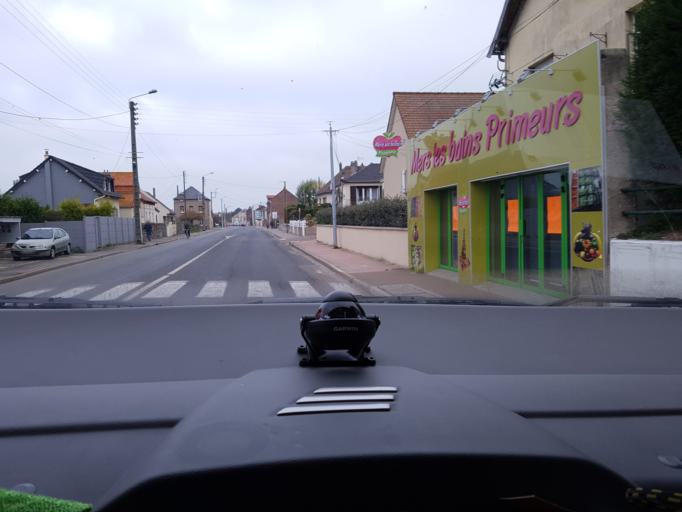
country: FR
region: Picardie
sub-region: Departement de la Somme
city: Mers-les-Bains
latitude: 50.0630
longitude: 1.4018
